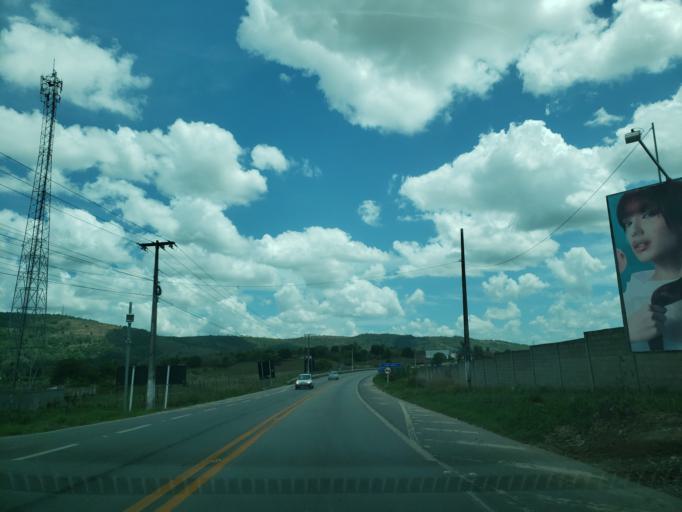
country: BR
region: Alagoas
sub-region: Uniao Dos Palmares
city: Uniao dos Palmares
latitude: -9.1518
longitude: -36.0131
